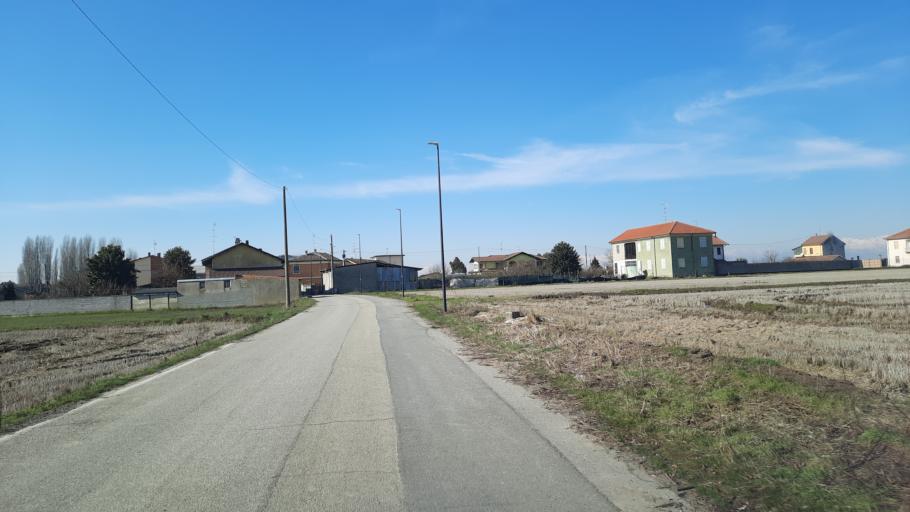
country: IT
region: Piedmont
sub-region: Provincia di Vercelli
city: Pertengo
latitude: 45.2379
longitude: 8.4176
